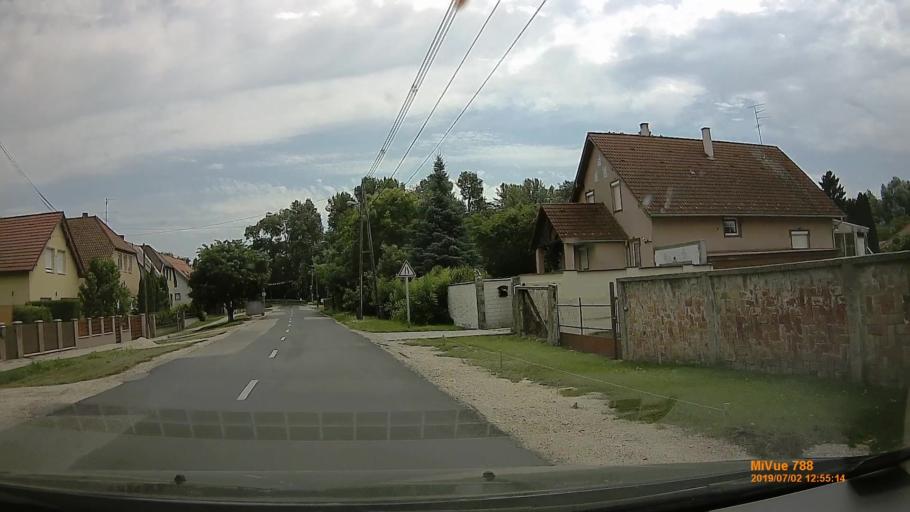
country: HU
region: Gyor-Moson-Sopron
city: Mosonmagyarovar
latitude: 47.8576
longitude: 17.2884
